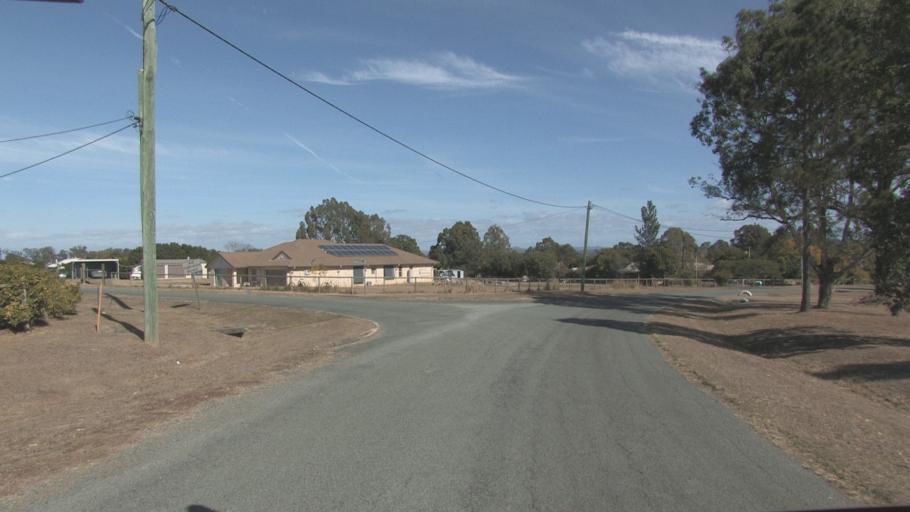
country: AU
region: Queensland
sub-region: Logan
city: Cedar Vale
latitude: -27.8705
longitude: 152.9724
